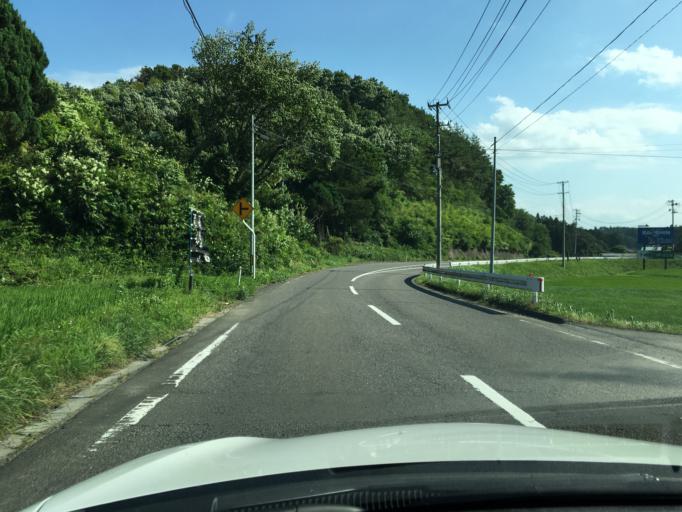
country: JP
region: Fukushima
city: Ishikawa
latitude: 37.2171
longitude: 140.5438
